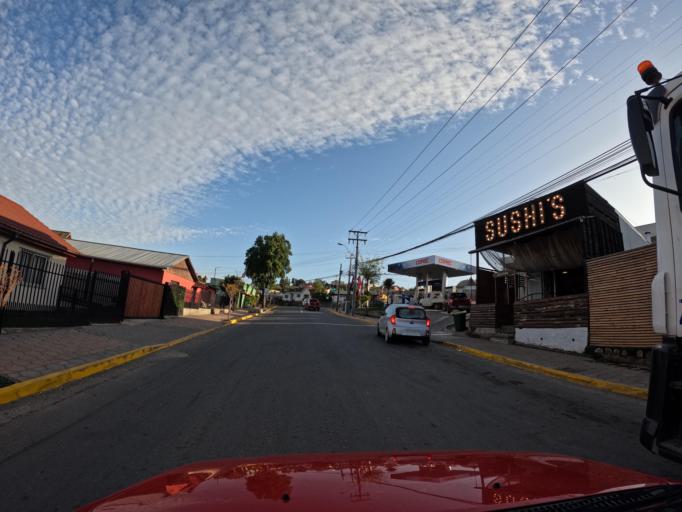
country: CL
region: Valparaiso
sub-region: San Antonio Province
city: San Antonio
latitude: -34.1170
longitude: -71.7296
